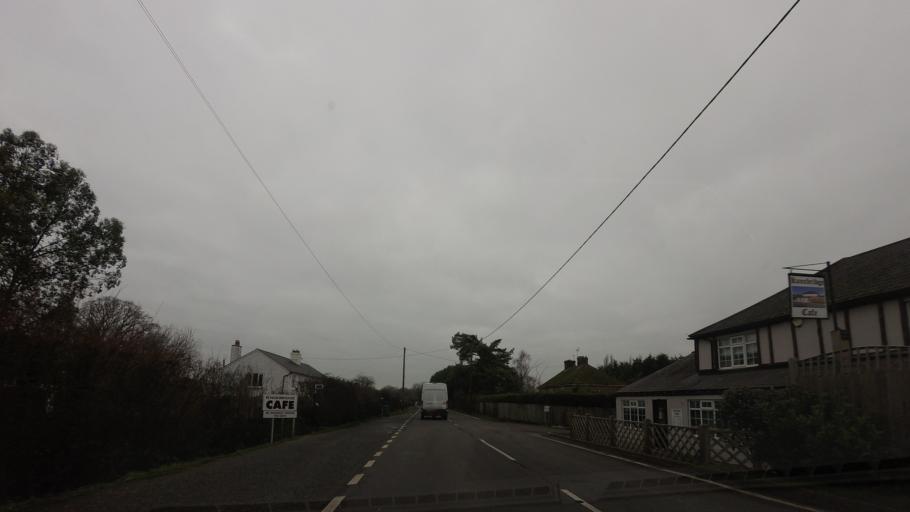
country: GB
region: England
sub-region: Kent
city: Staplehurst
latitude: 51.1375
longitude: 0.5553
